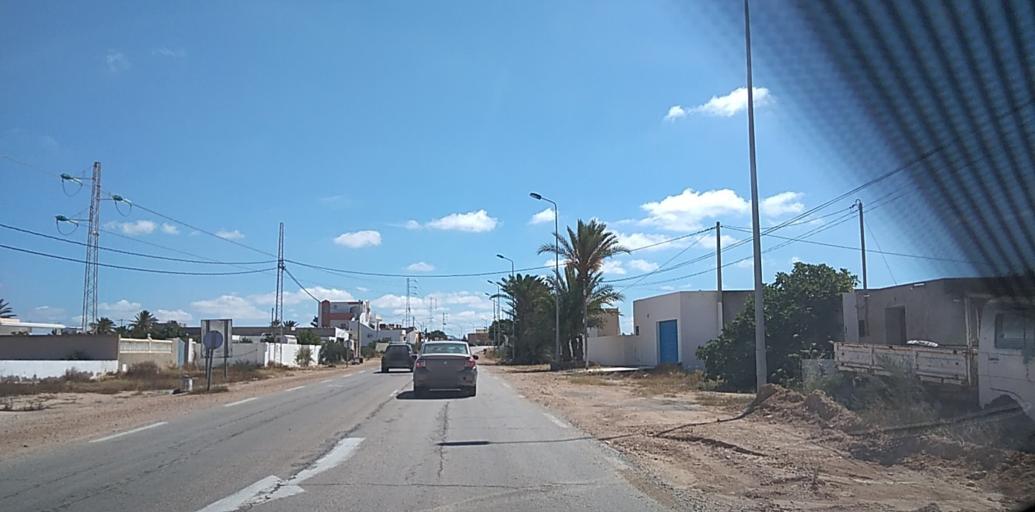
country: TN
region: Safaqis
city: Al Qarmadah
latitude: 34.6649
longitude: 11.1279
